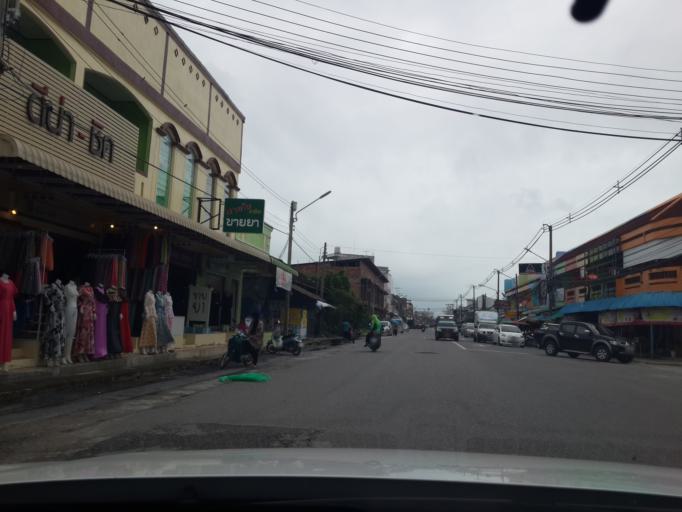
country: TH
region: Pattani
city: Pattani
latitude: 6.8597
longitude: 101.2524
